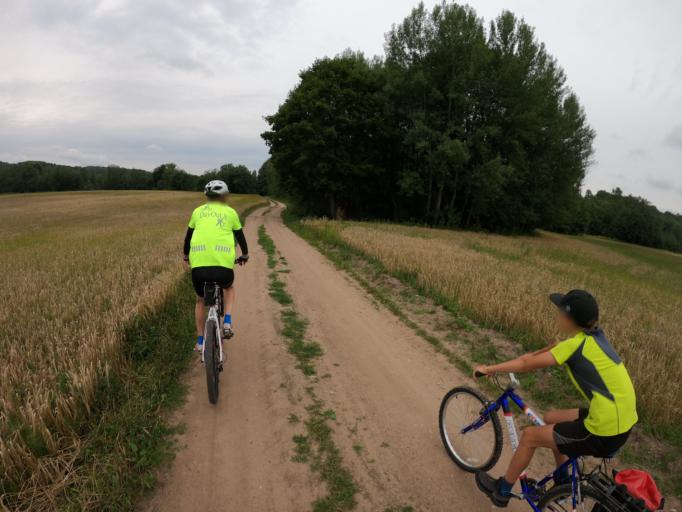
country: LT
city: Ariogala
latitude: 55.3663
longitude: 23.3181
